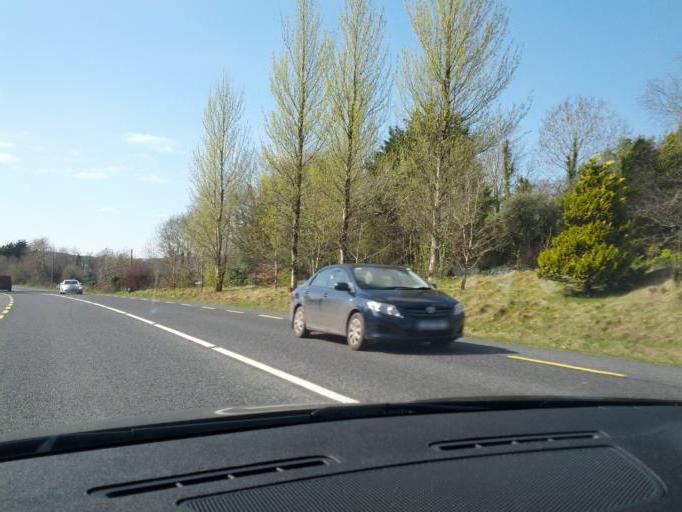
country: IE
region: Connaught
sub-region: County Galway
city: Moycullen
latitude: 53.3091
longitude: -9.1284
